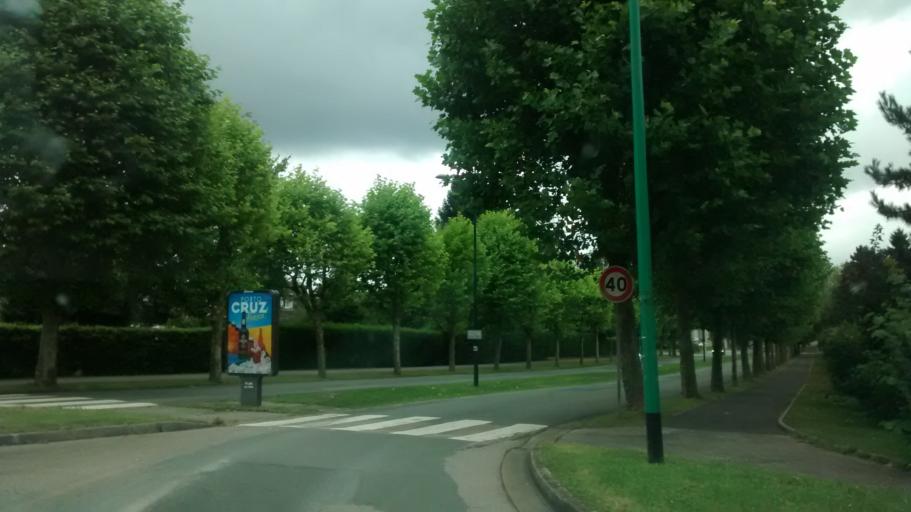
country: FR
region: Haute-Normandie
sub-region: Departement de la Seine-Maritime
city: Bois-Guillaume
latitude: 49.4672
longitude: 1.1415
